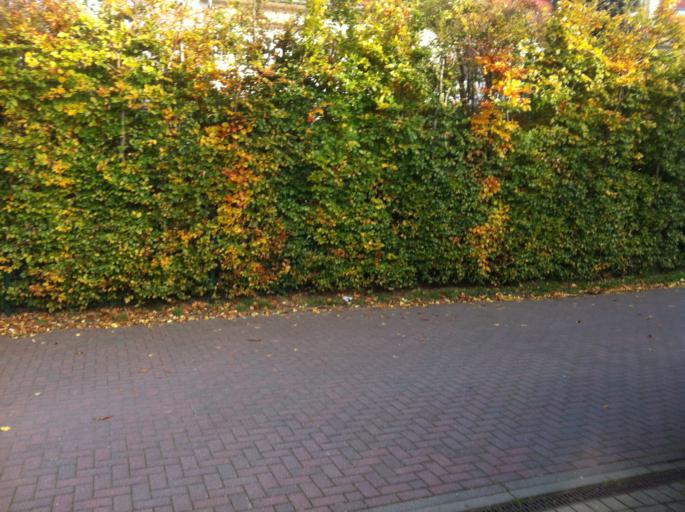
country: DE
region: Hamburg
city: Stellingen
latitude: 53.5758
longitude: 9.9330
